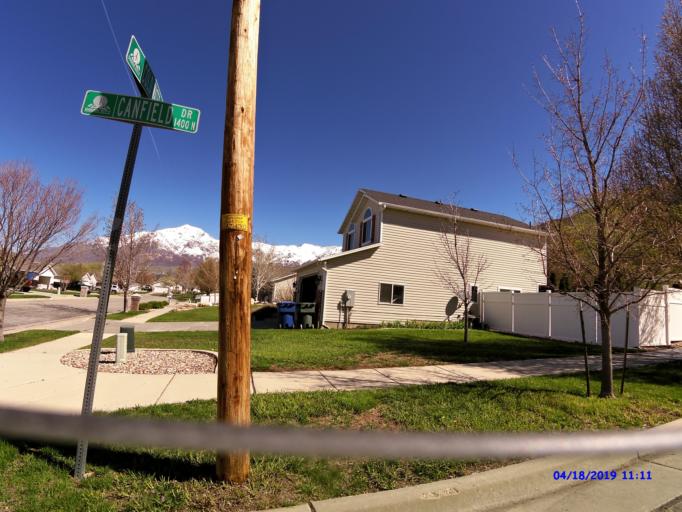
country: US
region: Utah
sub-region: Weber County
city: North Ogden
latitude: 41.2832
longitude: -111.9525
